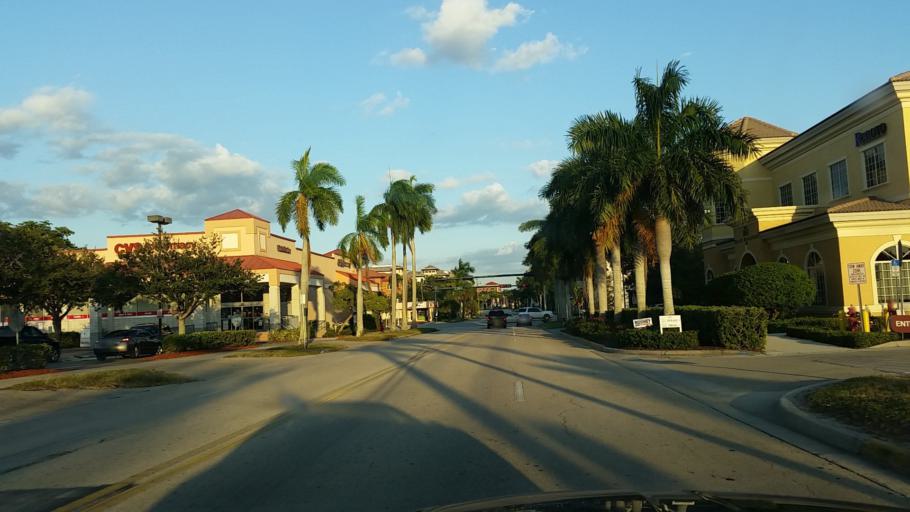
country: US
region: Florida
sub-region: Collier County
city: Naples
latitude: 26.1439
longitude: -81.7963
